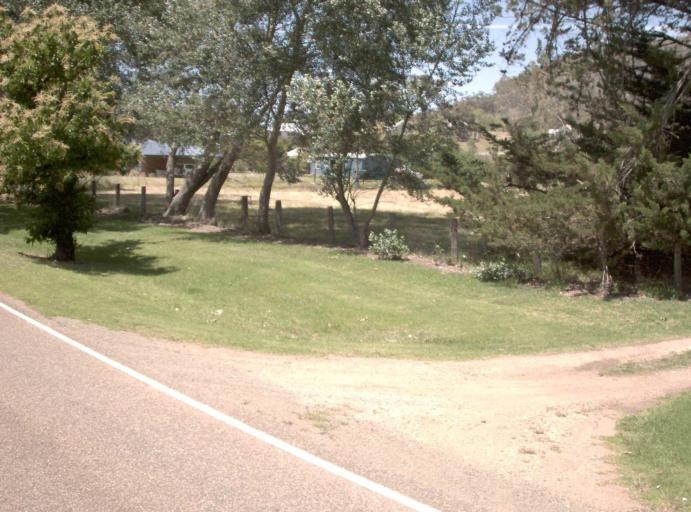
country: AU
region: Victoria
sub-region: East Gippsland
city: Bairnsdale
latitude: -37.2615
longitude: 147.7192
